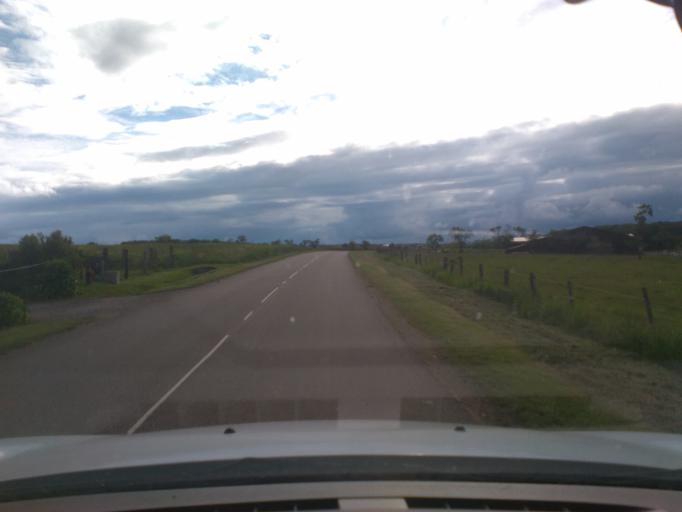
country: FR
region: Lorraine
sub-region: Departement des Vosges
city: Mirecourt
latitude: 48.3300
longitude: 6.0542
